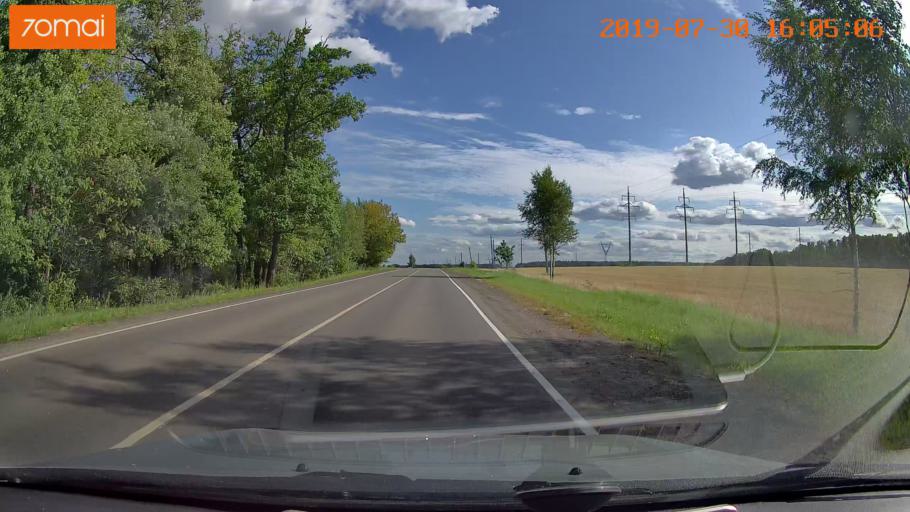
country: RU
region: Moskovskaya
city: Lopatinskiy
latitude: 55.2711
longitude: 38.7137
